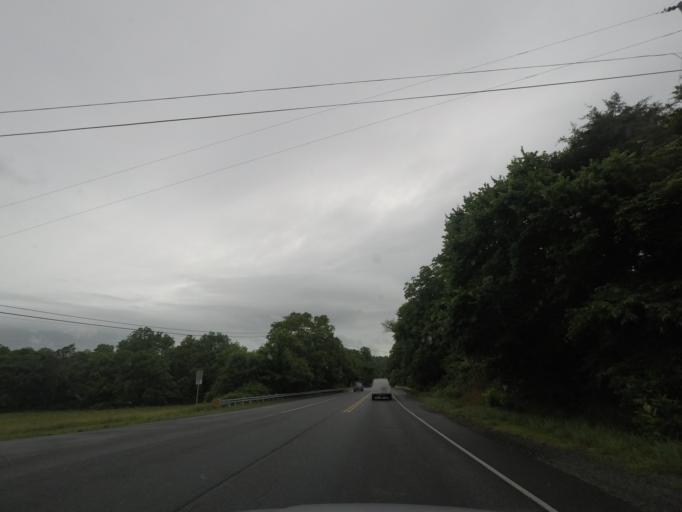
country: US
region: Virginia
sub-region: Loudoun County
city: Brambleton
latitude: 39.0259
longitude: -77.6209
